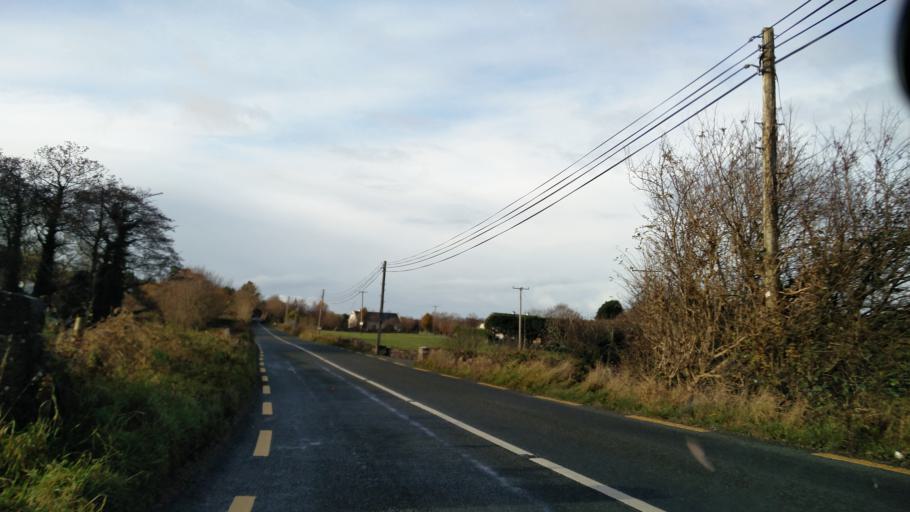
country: IE
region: Connaught
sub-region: Maigh Eo
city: Westport
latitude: 53.7851
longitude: -9.4824
